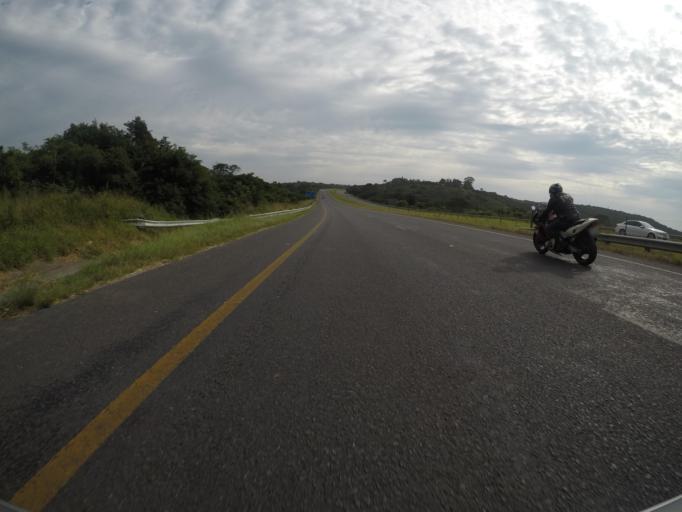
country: ZA
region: Eastern Cape
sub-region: Buffalo City Metropolitan Municipality
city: East London
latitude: -32.9458
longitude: 27.9410
